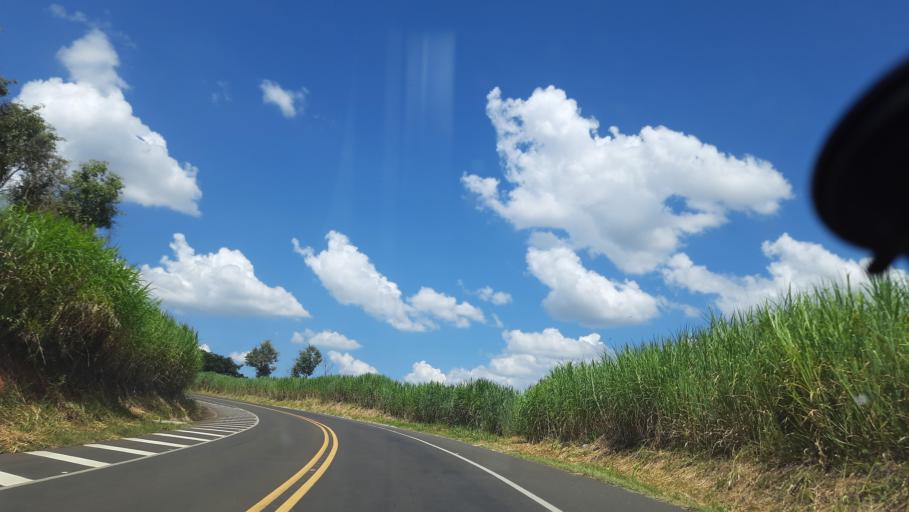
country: BR
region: Sao Paulo
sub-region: Sao Jose Do Rio Pardo
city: Sao Jose do Rio Pardo
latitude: -21.6078
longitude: -46.9646
